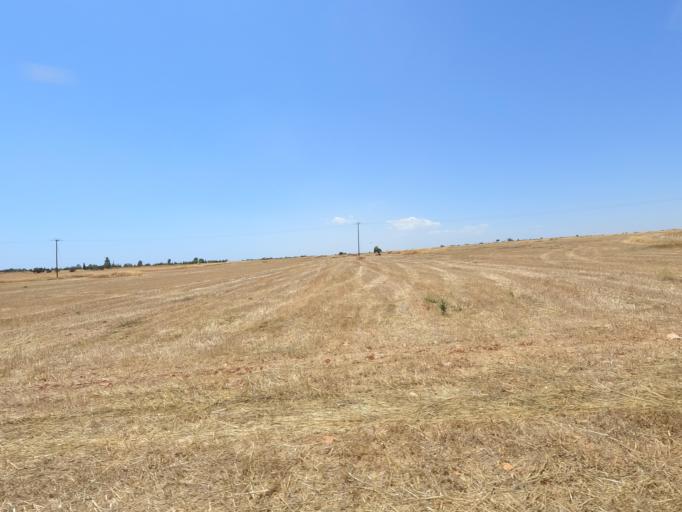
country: CY
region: Larnaka
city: Pergamos
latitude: 35.0224
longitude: 33.7148
